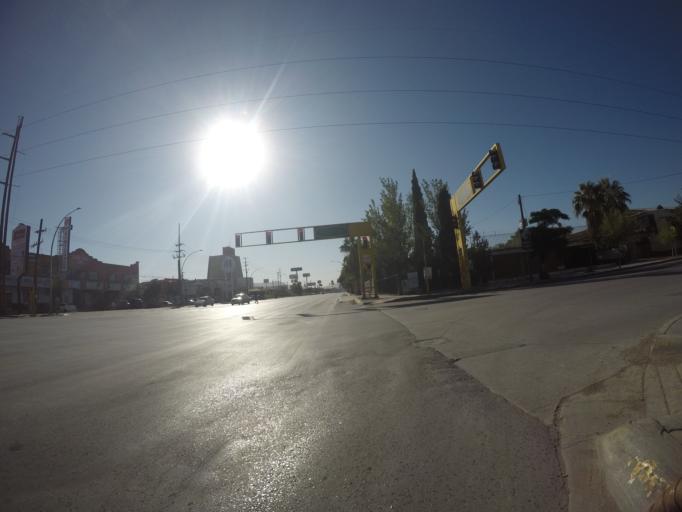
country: MX
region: Chihuahua
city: Ciudad Juarez
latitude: 31.7377
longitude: -106.4408
